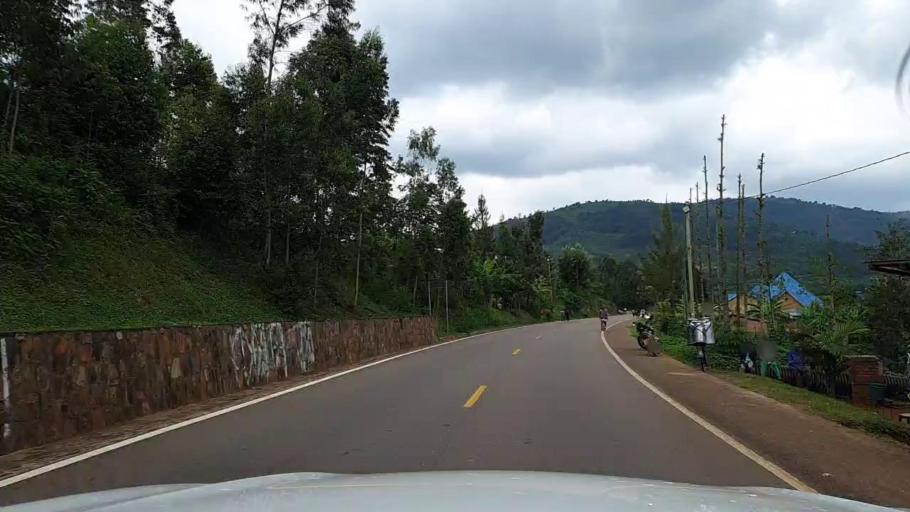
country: RW
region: Northern Province
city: Byumba
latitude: -1.6800
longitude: 30.1008
